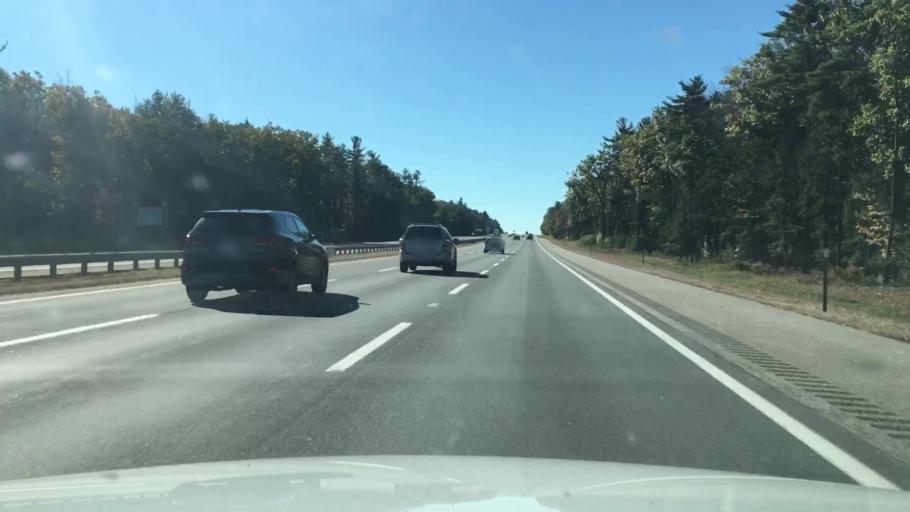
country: US
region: Maine
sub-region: York County
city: Ogunquit
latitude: 43.2879
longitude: -70.6170
